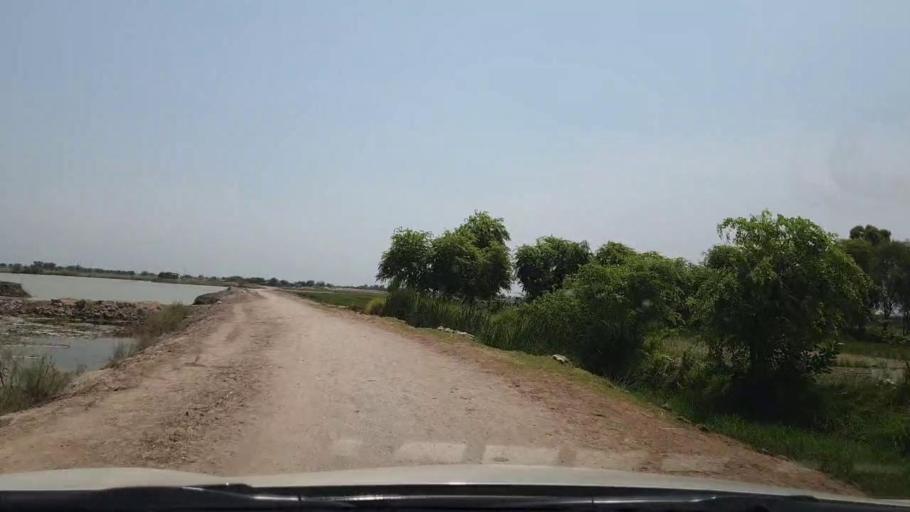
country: PK
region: Sindh
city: Ratodero
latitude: 27.8083
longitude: 68.2438
